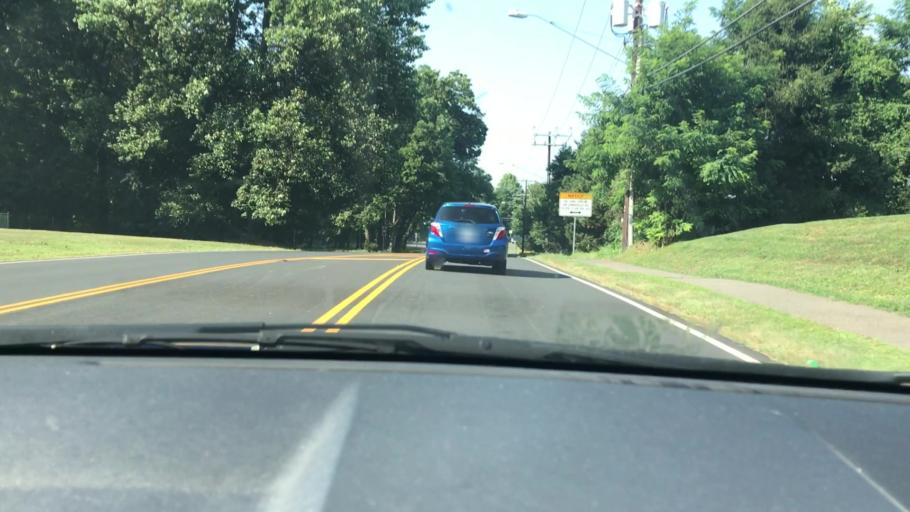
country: US
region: Virginia
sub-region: Fairfax County
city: Tysons Corner
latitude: 38.9370
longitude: -77.2321
